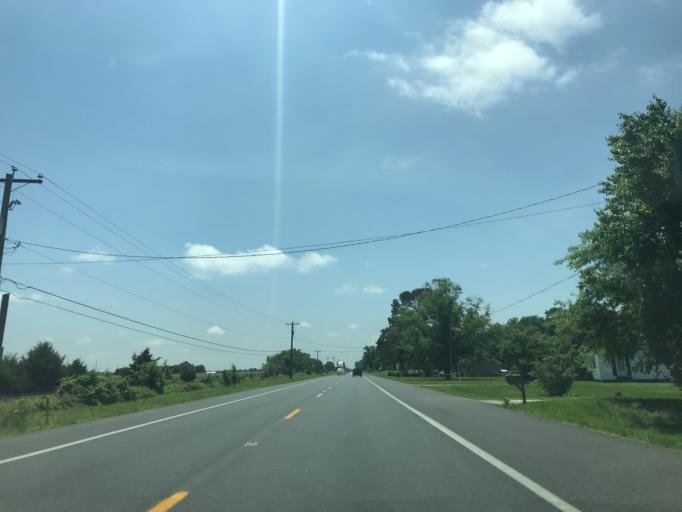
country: US
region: Maryland
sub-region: Dorchester County
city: Hurlock
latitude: 38.6099
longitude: -75.8982
